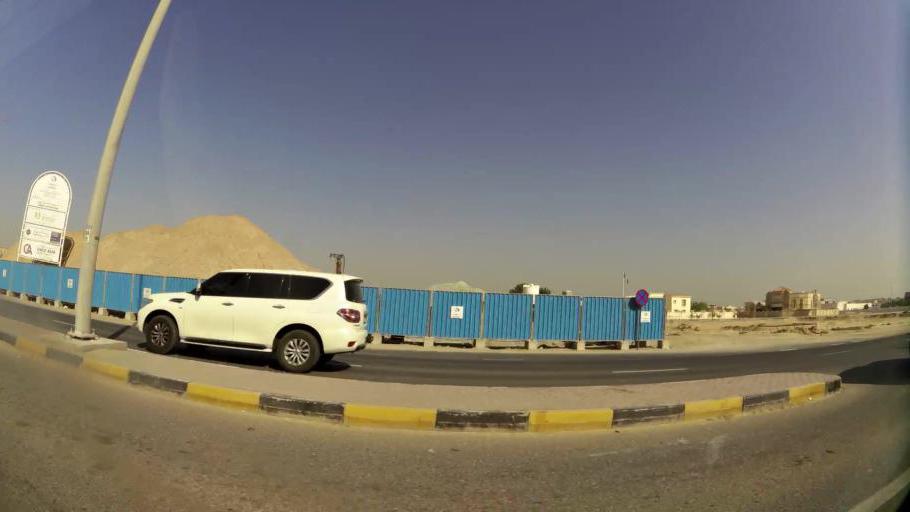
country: AE
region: Ajman
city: Ajman
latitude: 25.4045
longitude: 55.5064
